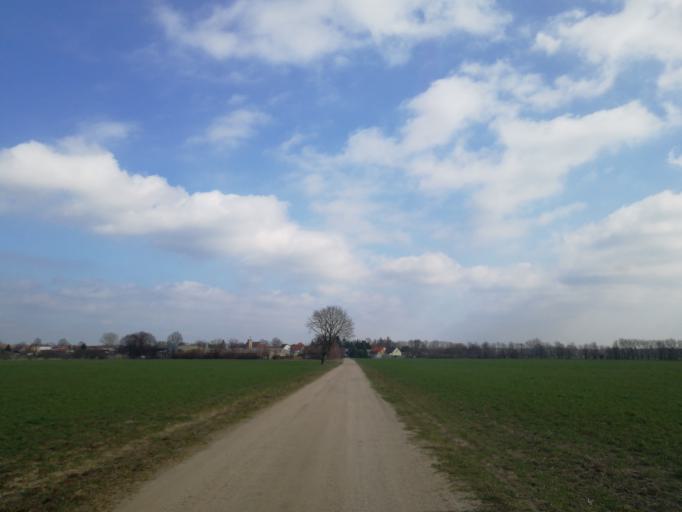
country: DE
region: Brandenburg
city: Finsterwalde
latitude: 51.6611
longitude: 13.7318
